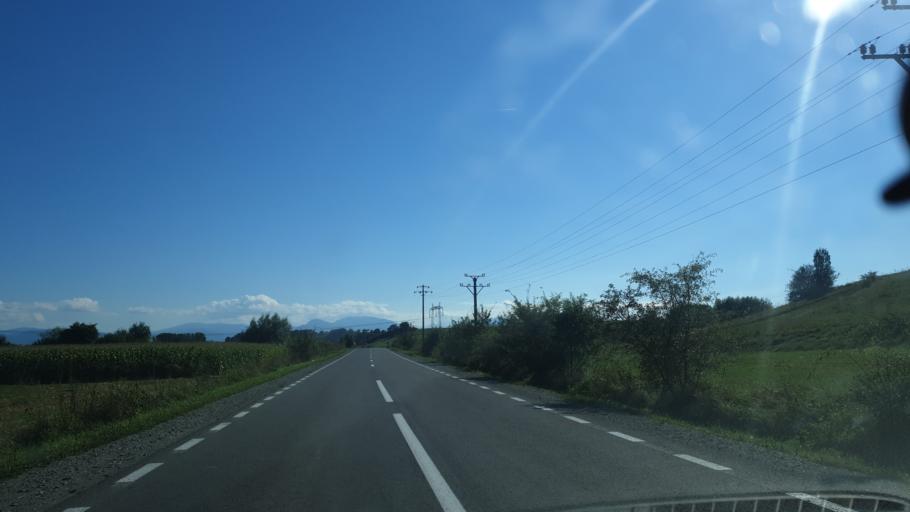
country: RO
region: Covasna
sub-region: Comuna Ilieni
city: Ilieni
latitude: 45.8112
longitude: 25.7733
